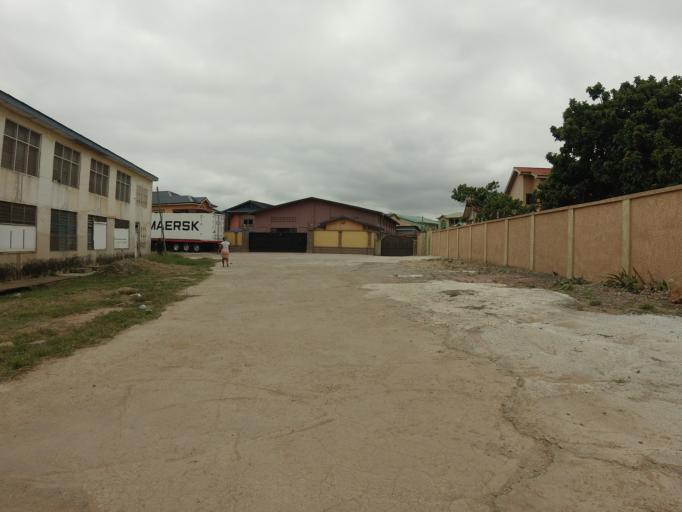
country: GH
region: Greater Accra
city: Dome
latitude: 5.6354
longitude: -0.2363
